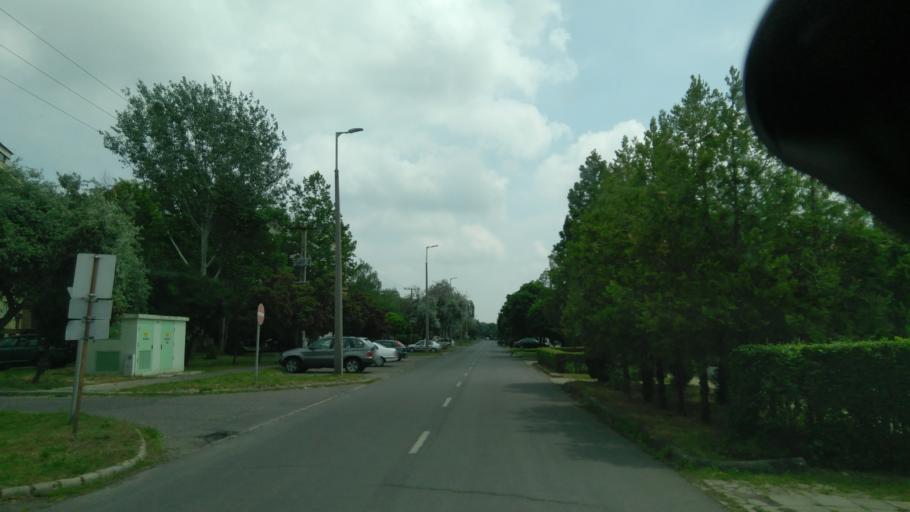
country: HU
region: Bekes
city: Gyula
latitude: 46.6555
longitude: 21.2603
